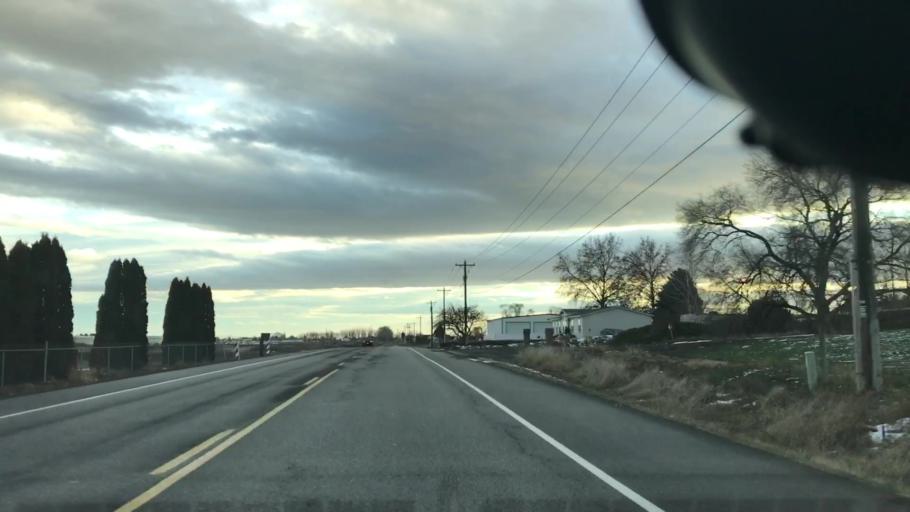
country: US
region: Washington
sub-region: Grant County
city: Moses Lake
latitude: 47.1060
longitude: -119.2361
